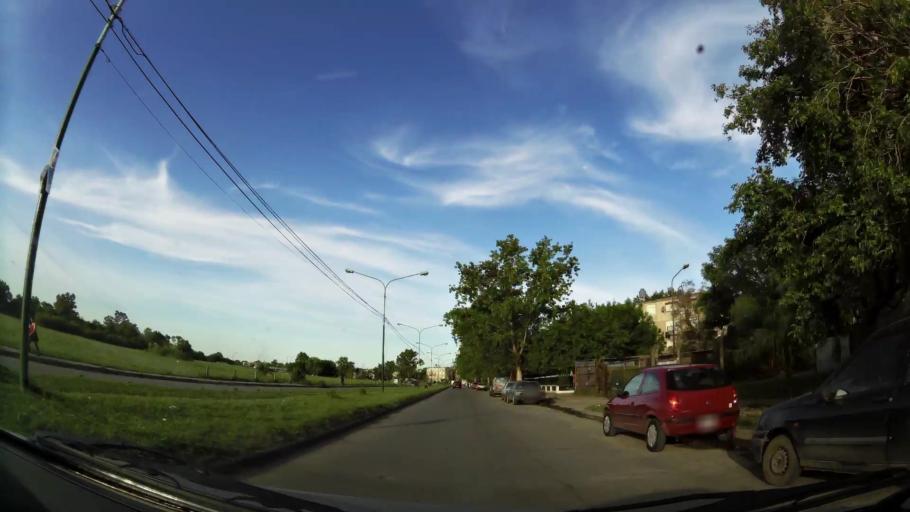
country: AR
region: Buenos Aires
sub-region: Partido de Almirante Brown
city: Adrogue
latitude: -34.8172
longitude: -58.3385
